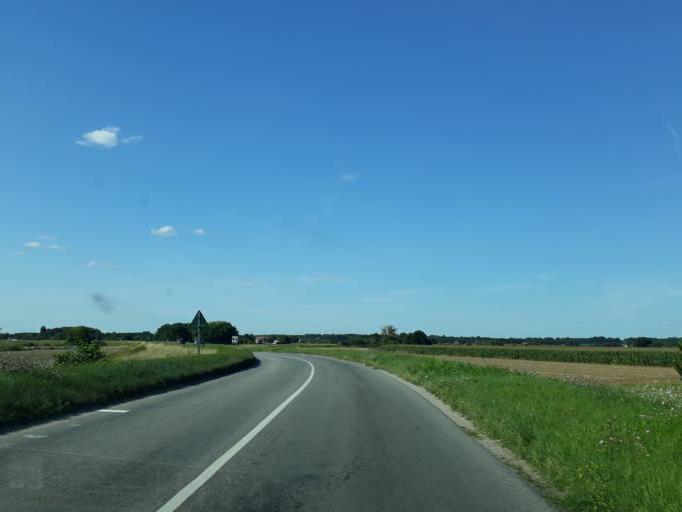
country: FR
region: Centre
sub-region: Departement du Loiret
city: Saint-Benoit-sur-Loire
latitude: 47.8177
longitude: 2.3002
